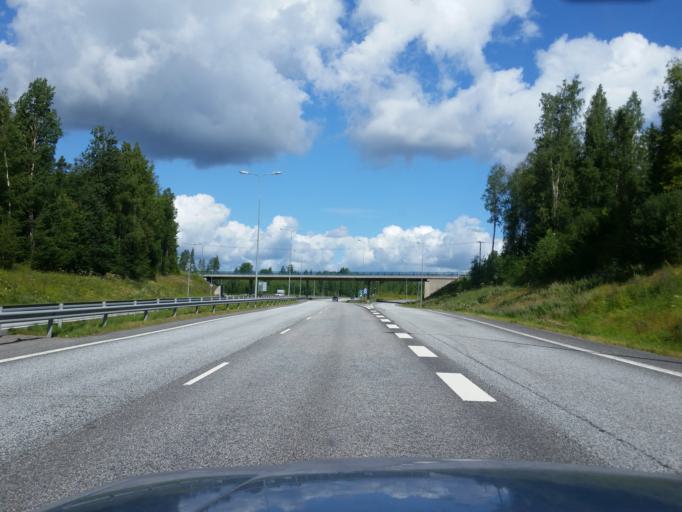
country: FI
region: Uusimaa
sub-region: Helsinki
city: Vihti
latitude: 60.3004
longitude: 24.3579
